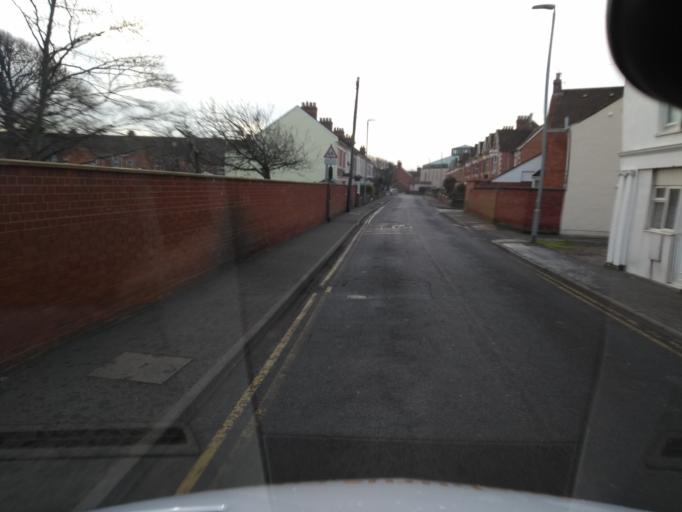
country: GB
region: England
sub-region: Somerset
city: Burnham-on-Sea
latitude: 51.2340
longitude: -2.9938
